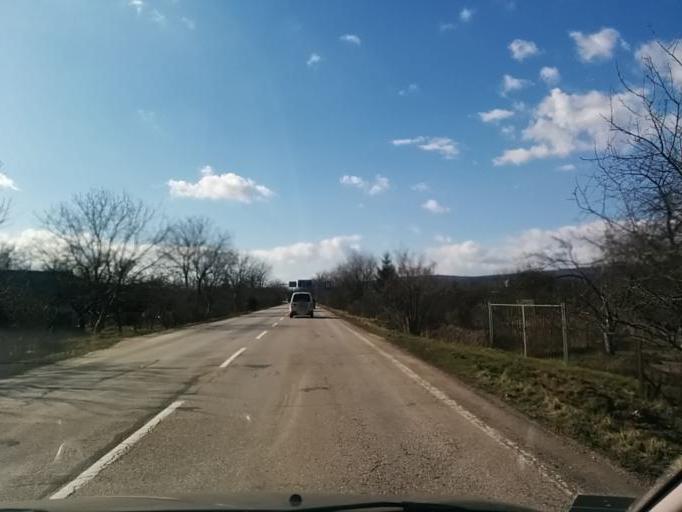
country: SK
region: Trenciansky
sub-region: Okres Nove Mesto nad Vahom
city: Nove Mesto nad Vahom
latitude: 48.7701
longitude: 17.8479
